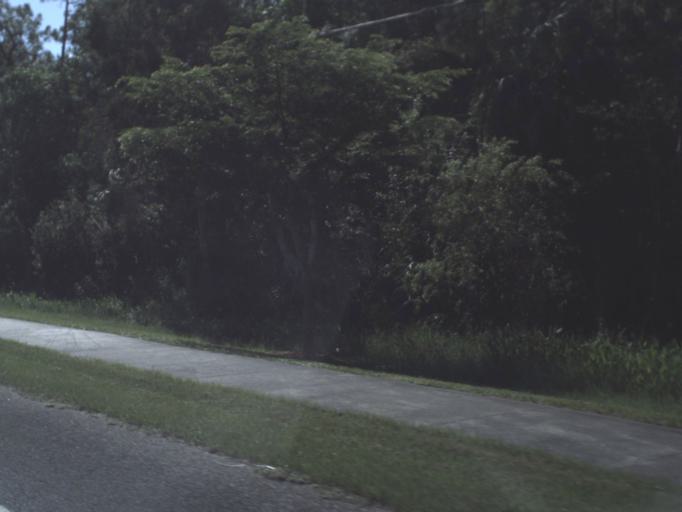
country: US
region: Florida
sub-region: Collier County
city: Lely Resort
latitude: 26.0721
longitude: -81.7132
